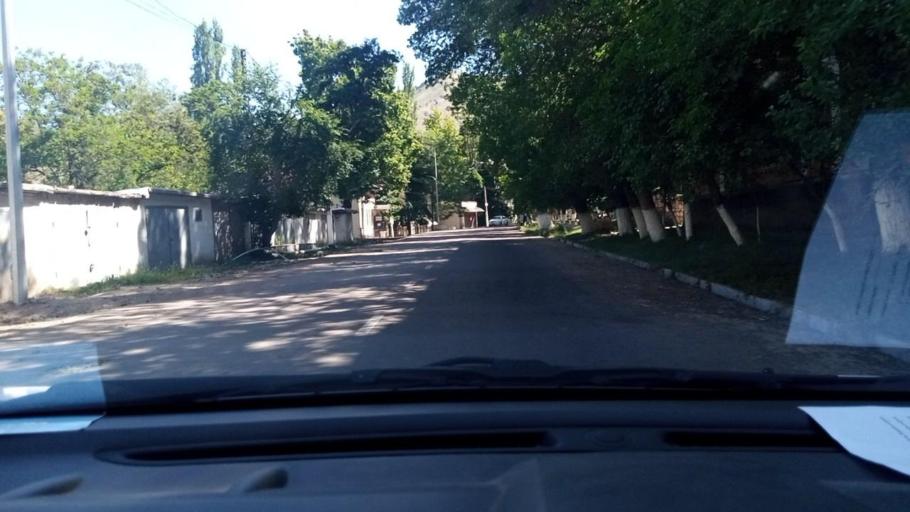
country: UZ
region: Toshkent
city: Yangiobod
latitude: 41.1177
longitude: 70.0909
